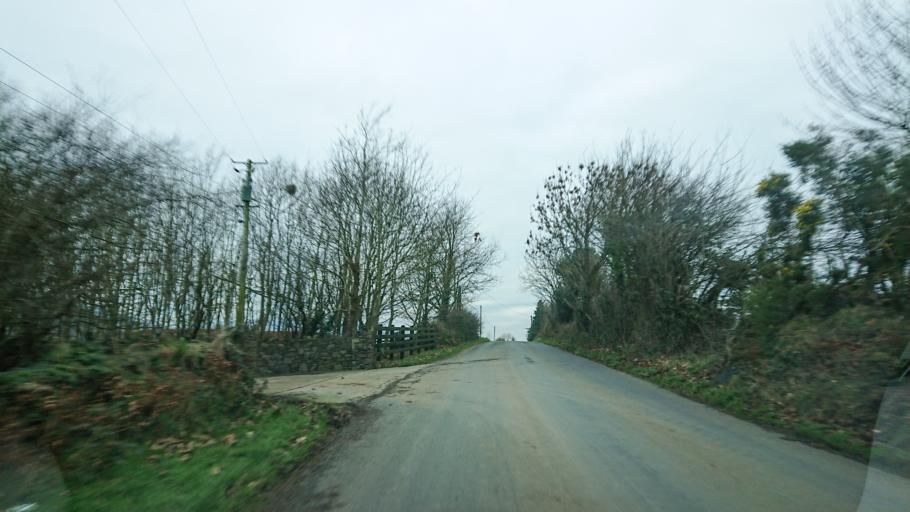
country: IE
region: Munster
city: Carrick-on-Suir
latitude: 52.2767
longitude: -7.4243
